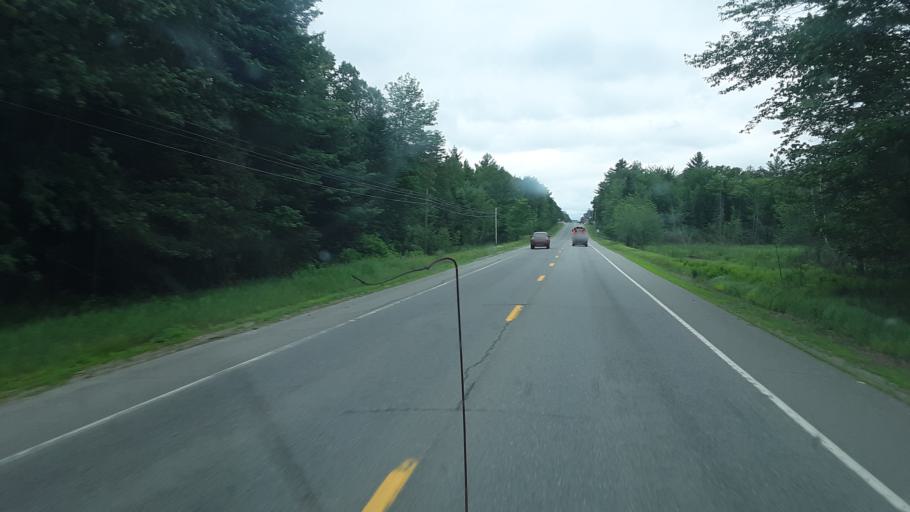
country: US
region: Maine
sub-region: Penobscot County
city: Millinocket
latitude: 45.6570
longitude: -68.6713
